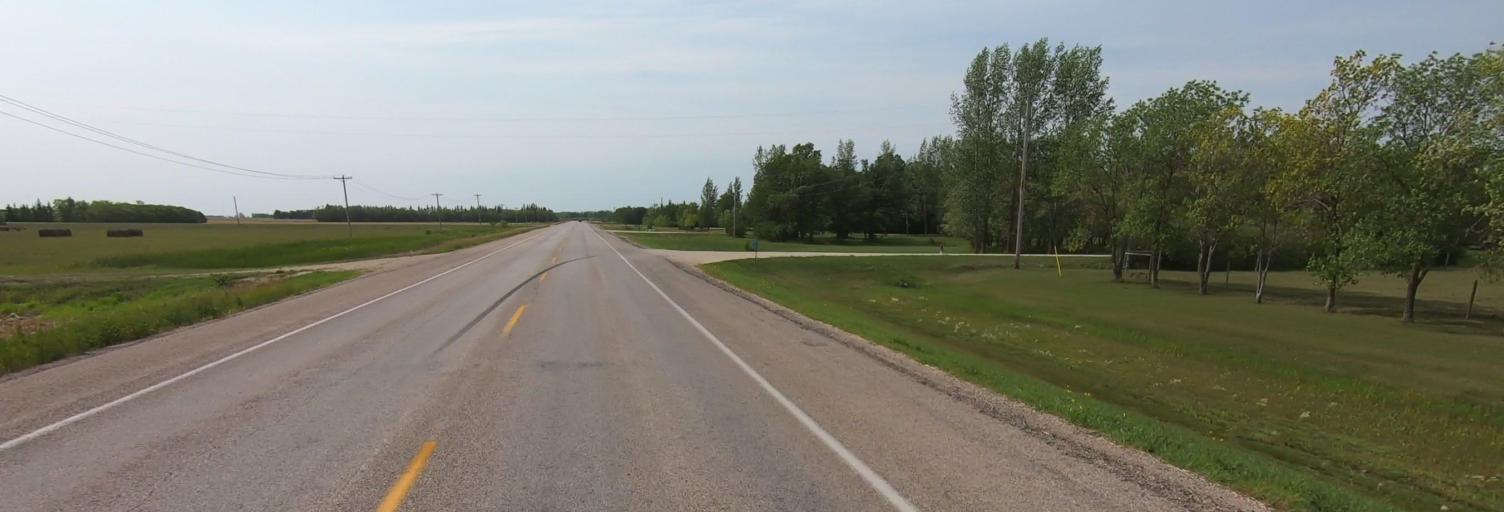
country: CA
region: Manitoba
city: Niverville
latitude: 49.6430
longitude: -97.1049
